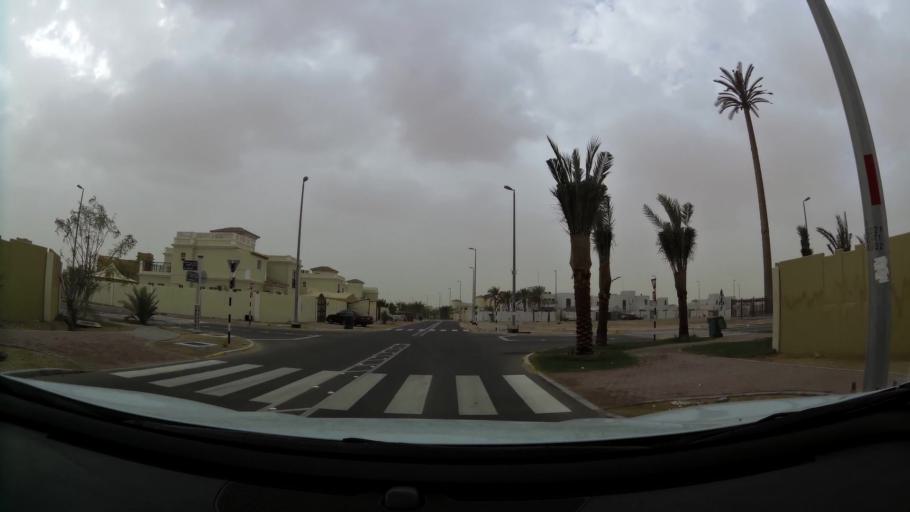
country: AE
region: Abu Dhabi
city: Abu Dhabi
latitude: 24.4425
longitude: 54.7126
